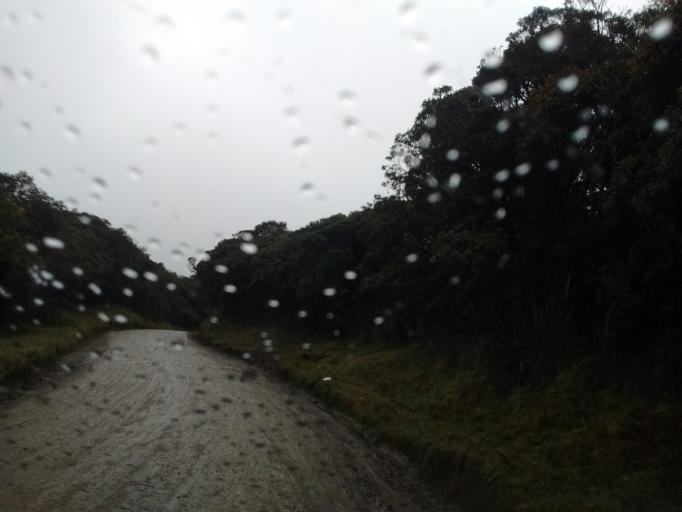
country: CO
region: Cauca
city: Paispamba
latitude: 2.1663
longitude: -76.4033
